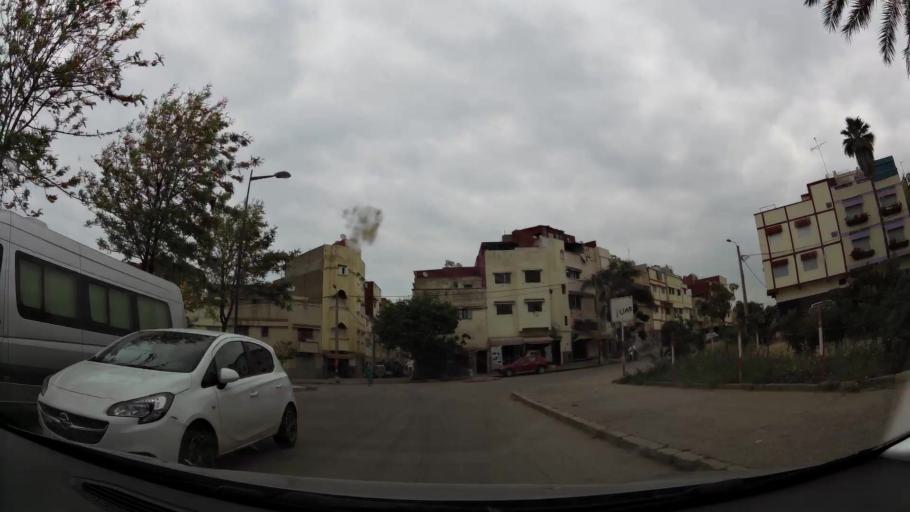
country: MA
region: Rabat-Sale-Zemmour-Zaer
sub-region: Rabat
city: Rabat
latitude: 33.9948
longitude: -6.8683
